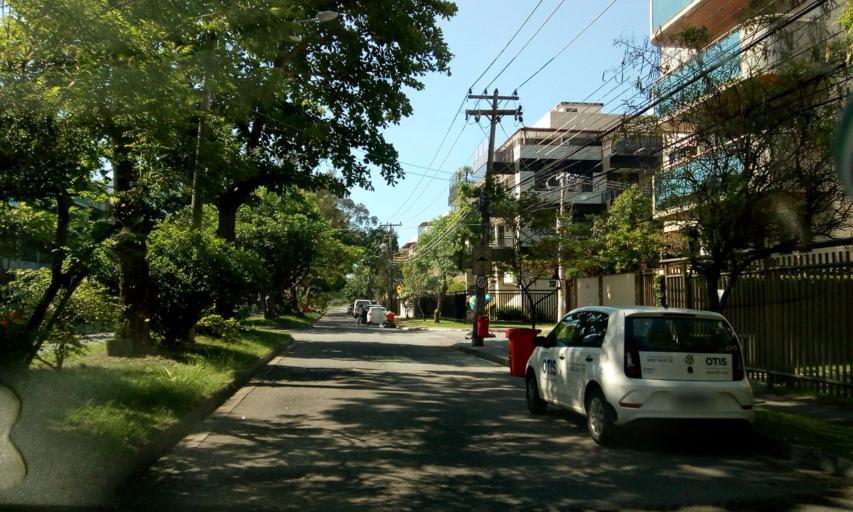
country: BR
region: Rio de Janeiro
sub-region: Nilopolis
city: Nilopolis
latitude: -23.0179
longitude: -43.4545
